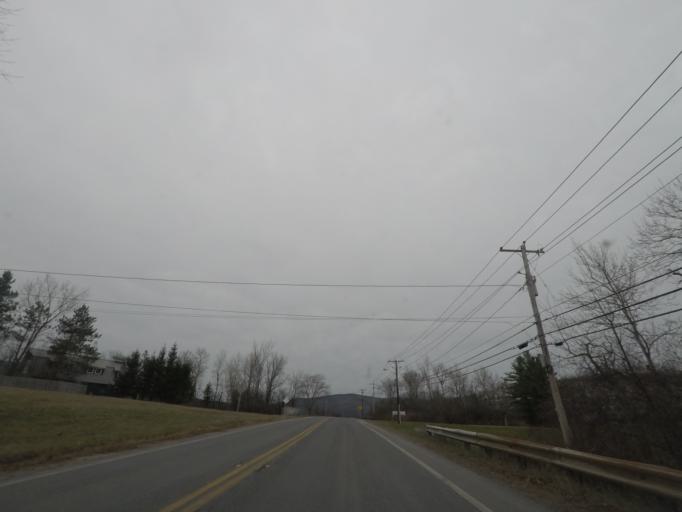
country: US
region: Massachusetts
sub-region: Berkshire County
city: Williamstown
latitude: 42.6772
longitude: -73.2350
